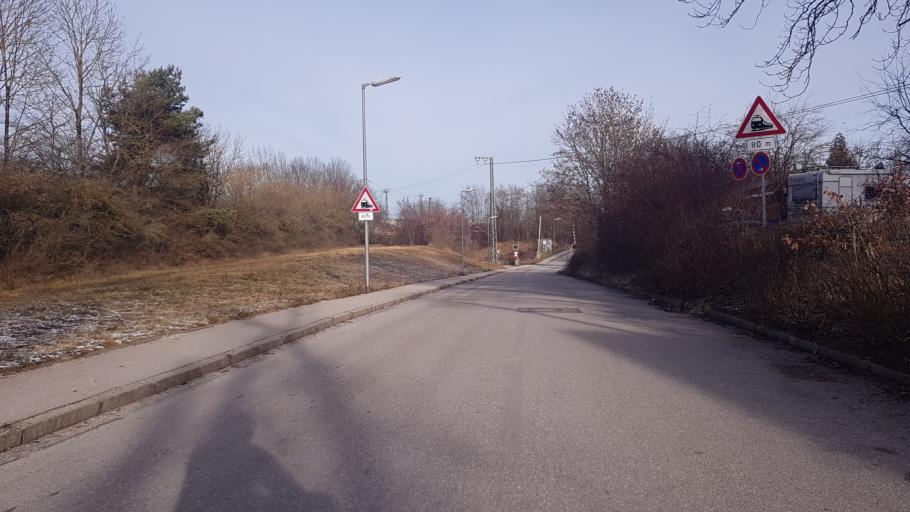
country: DE
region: Bavaria
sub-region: Upper Bavaria
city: Bogenhausen
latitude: 48.1326
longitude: 11.6535
